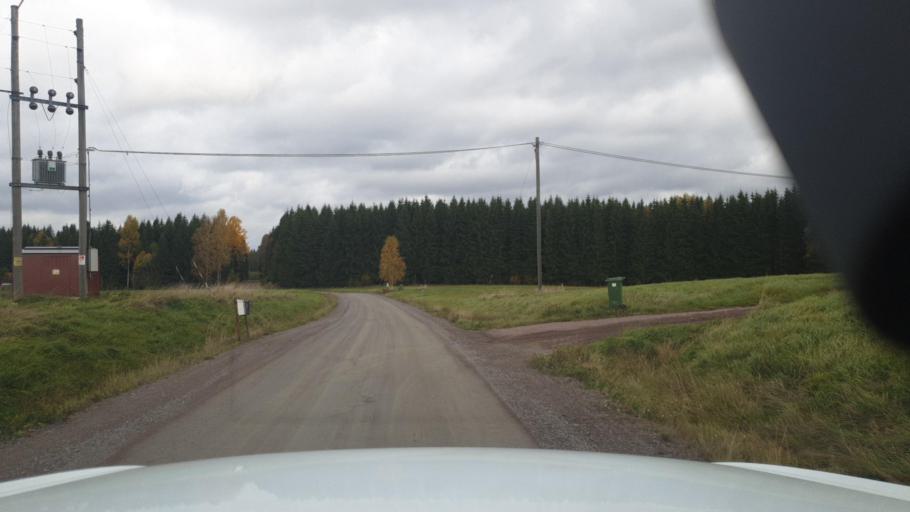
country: SE
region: Vaermland
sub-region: Sunne Kommun
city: Sunne
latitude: 59.8023
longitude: 13.0987
